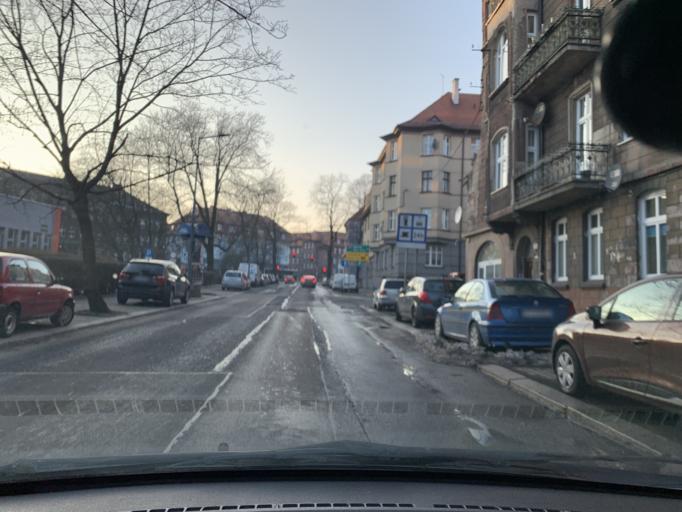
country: PL
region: Silesian Voivodeship
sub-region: Bytom
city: Bytom
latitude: 50.3513
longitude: 18.9151
